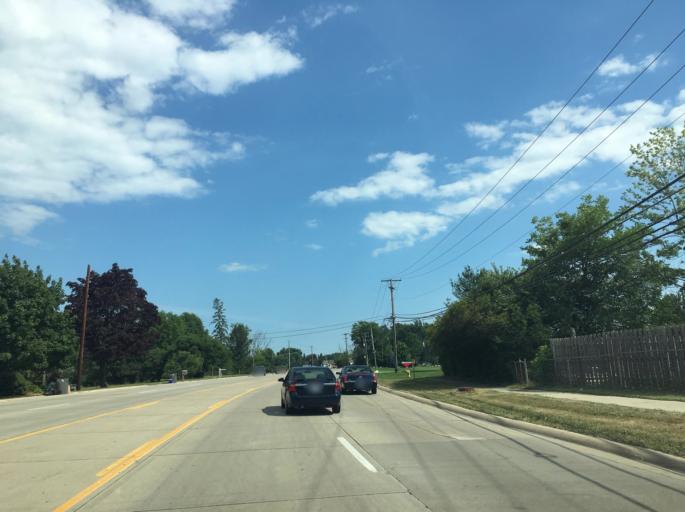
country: US
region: Michigan
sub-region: Macomb County
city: Clinton
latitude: 42.6087
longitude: -82.9235
